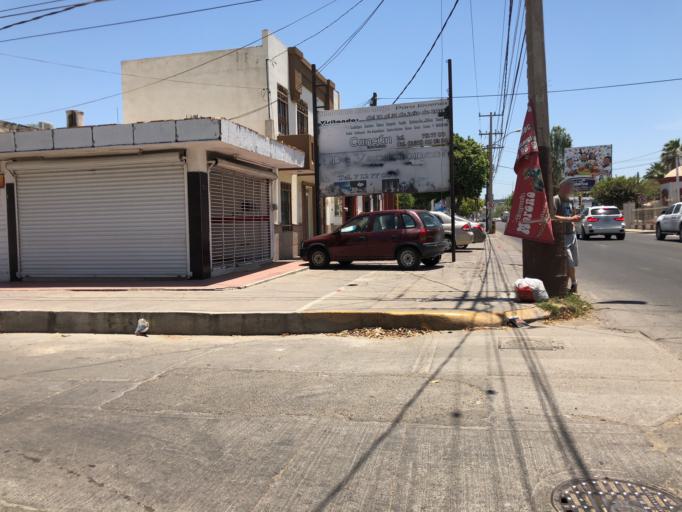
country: MX
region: Sinaloa
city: Culiacan
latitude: 24.8171
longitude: -107.3960
